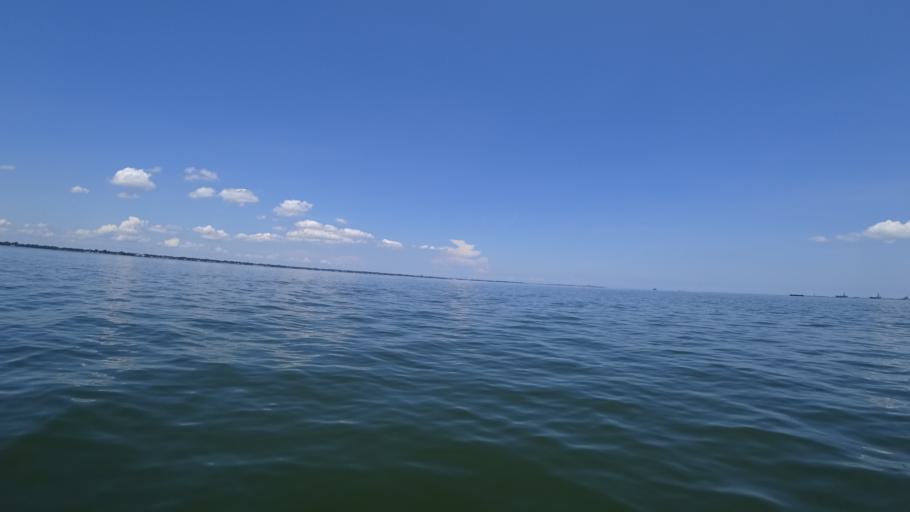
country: US
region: Virginia
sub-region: City of Newport News
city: Newport News
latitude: 36.9566
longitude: -76.3836
